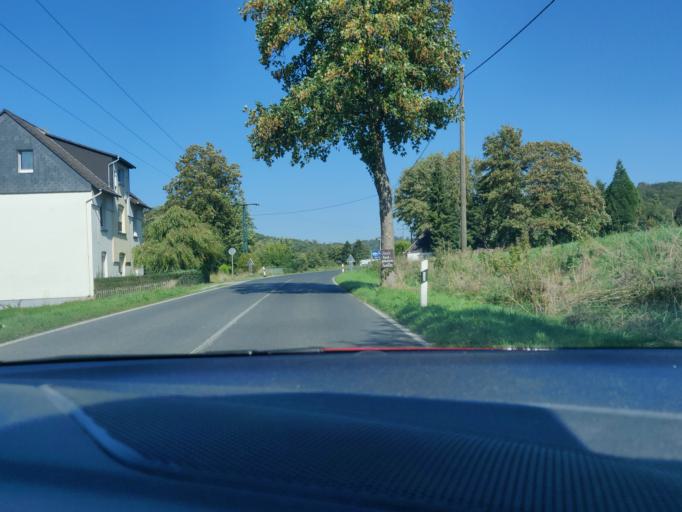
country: DE
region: North Rhine-Westphalia
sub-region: Regierungsbezirk Dusseldorf
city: Velbert
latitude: 51.3340
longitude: 7.0929
